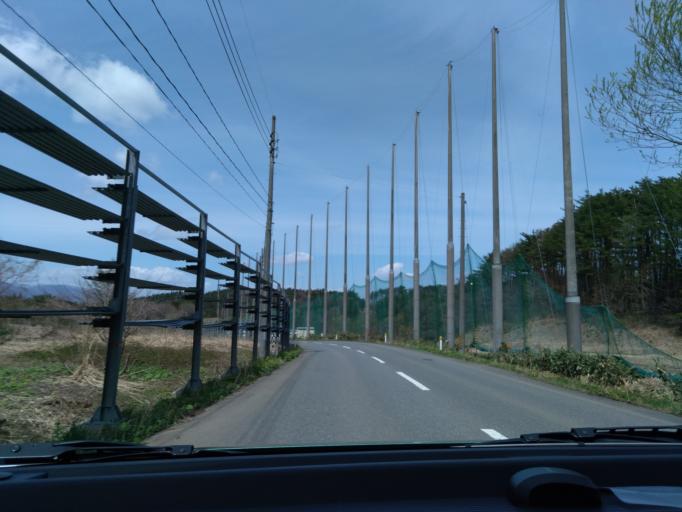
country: JP
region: Iwate
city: Kitakami
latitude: 39.2689
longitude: 140.9807
